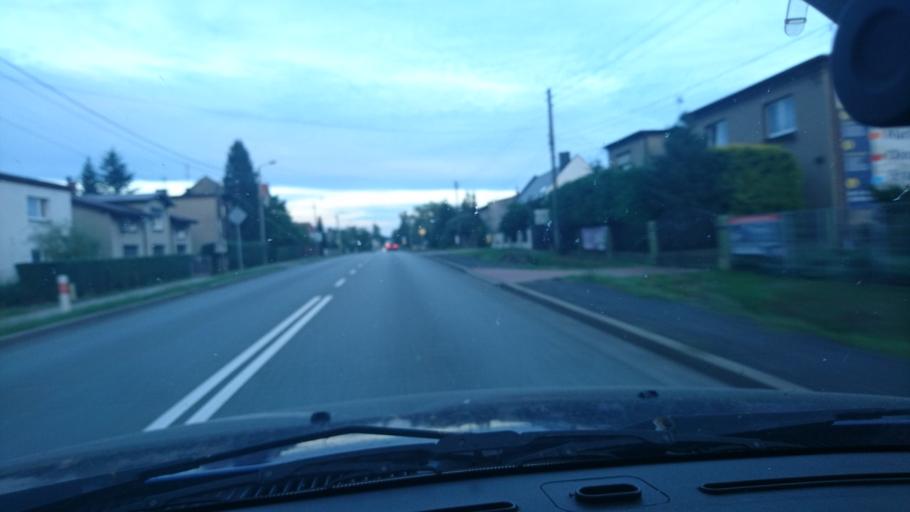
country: PL
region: Silesian Voivodeship
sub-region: Powiat tarnogorski
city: Tarnowskie Gory
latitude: 50.4704
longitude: 18.8067
